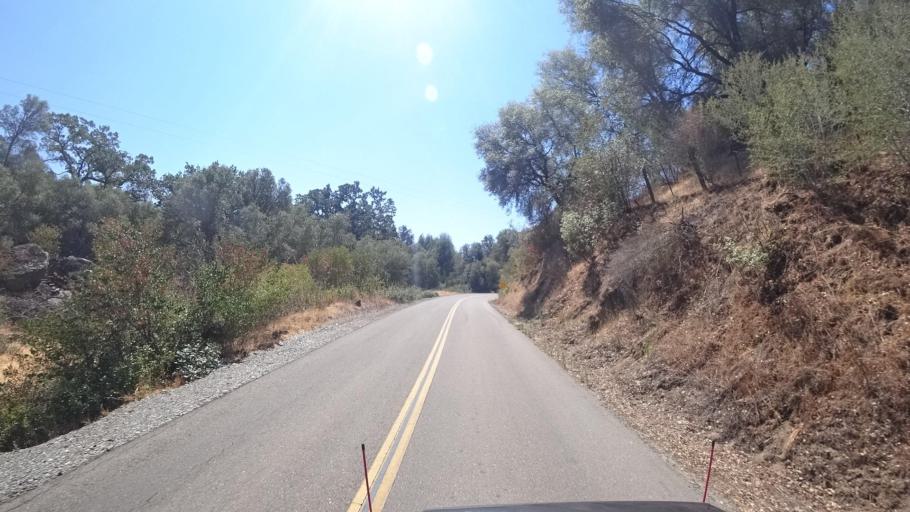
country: US
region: California
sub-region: Mariposa County
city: Mariposa
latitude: 37.4339
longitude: -119.9443
